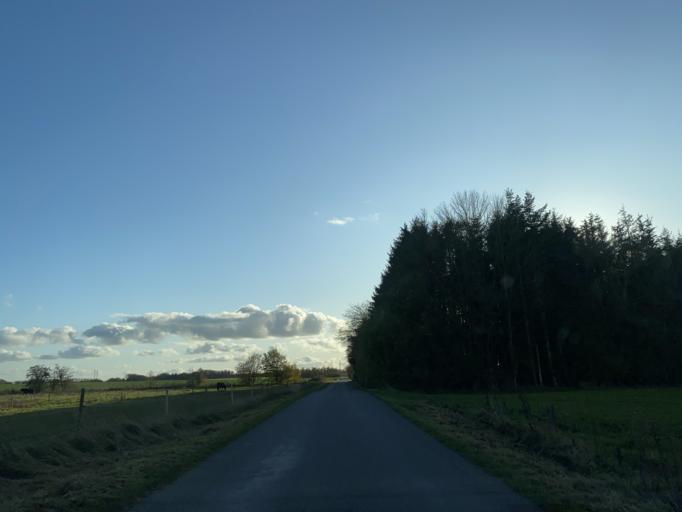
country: DK
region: Central Jutland
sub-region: Viborg Kommune
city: Bjerringbro
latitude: 56.3246
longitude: 9.7038
